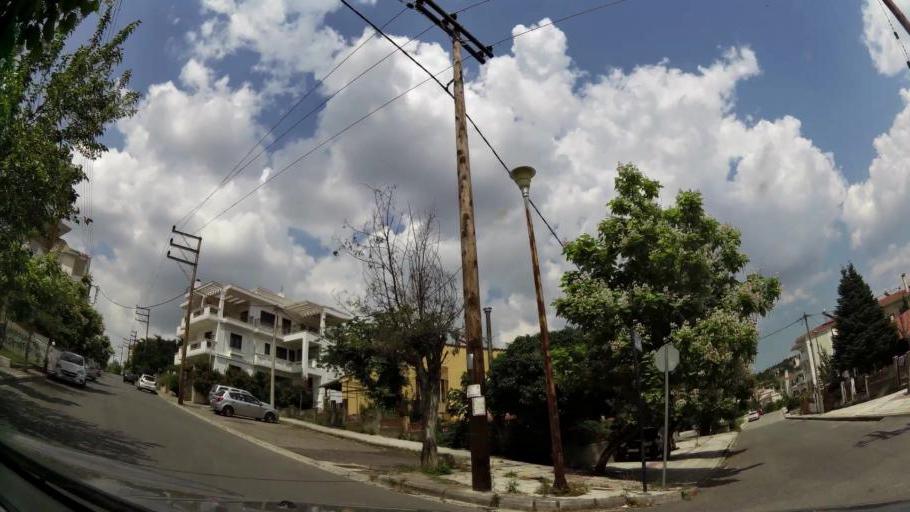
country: GR
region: West Macedonia
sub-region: Nomos Kozanis
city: Kozani
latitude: 40.3098
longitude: 21.7893
